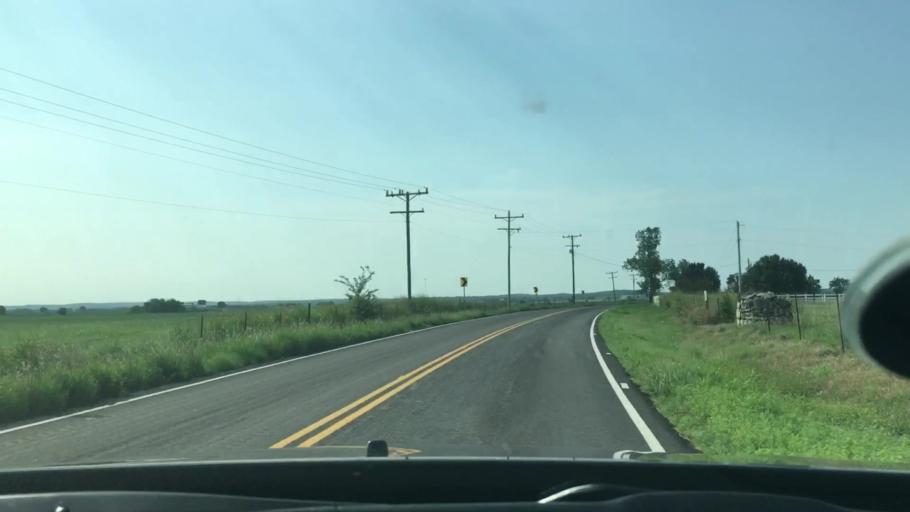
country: US
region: Oklahoma
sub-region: Bryan County
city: Durant
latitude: 34.1207
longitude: -96.4878
